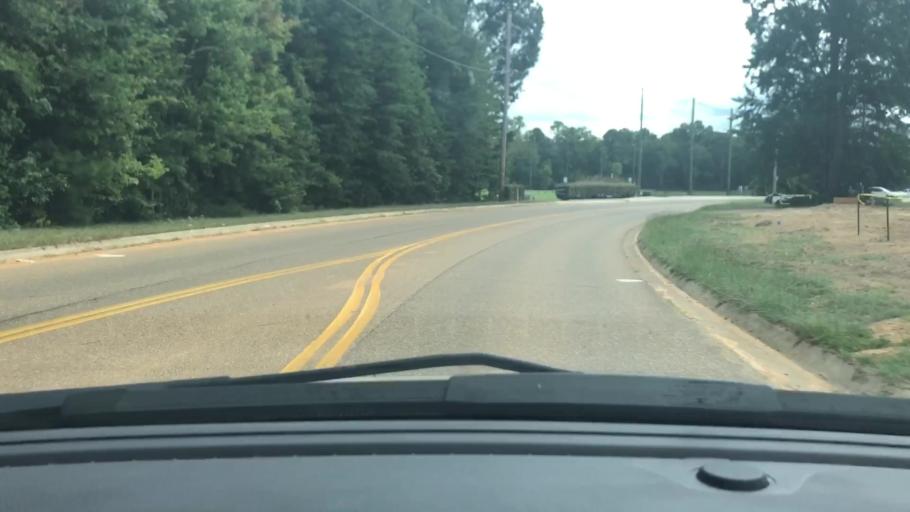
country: US
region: Arkansas
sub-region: Miller County
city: Texarkana
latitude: 33.4603
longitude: -94.0743
